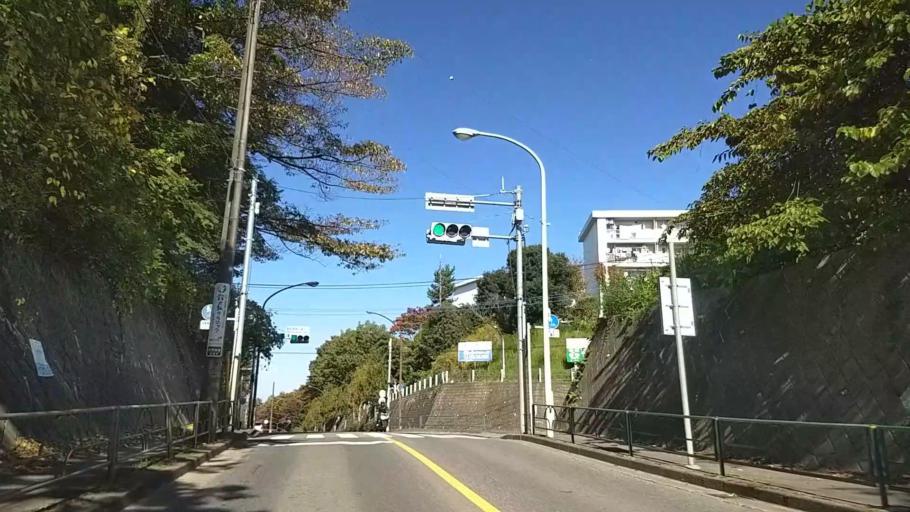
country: JP
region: Tokyo
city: Hachioji
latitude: 35.6220
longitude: 139.2872
